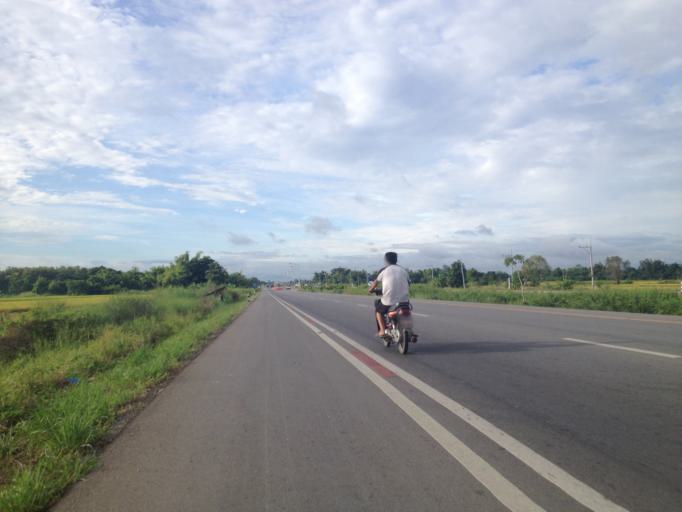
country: TH
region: Chiang Mai
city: San Pa Tong
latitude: 18.6273
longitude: 98.8389
